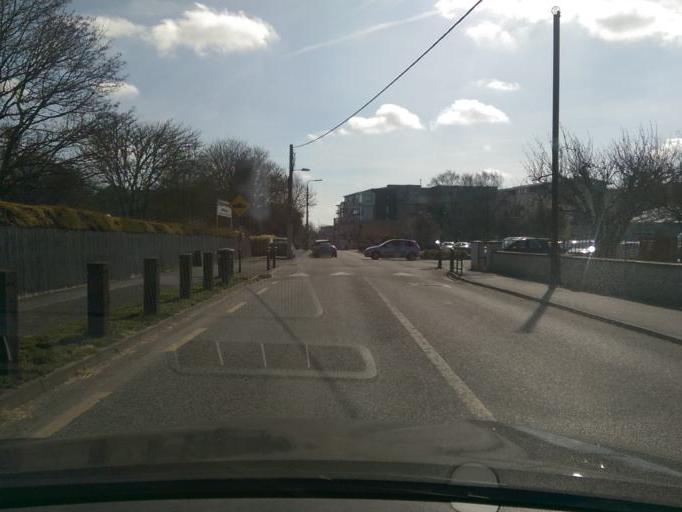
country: IE
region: Leinster
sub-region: Kildare
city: Maynooth
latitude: 53.3841
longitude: -6.5948
